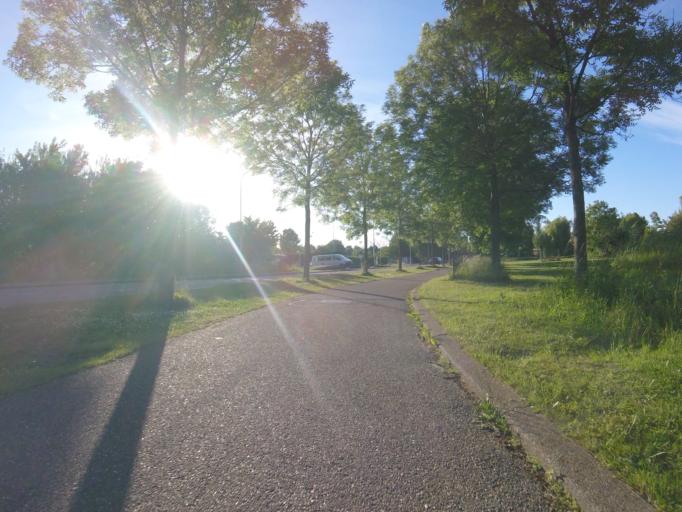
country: NL
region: North Holland
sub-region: Gemeente Haarlemmermeer
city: Hoofddorp
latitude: 52.3173
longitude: 4.6751
